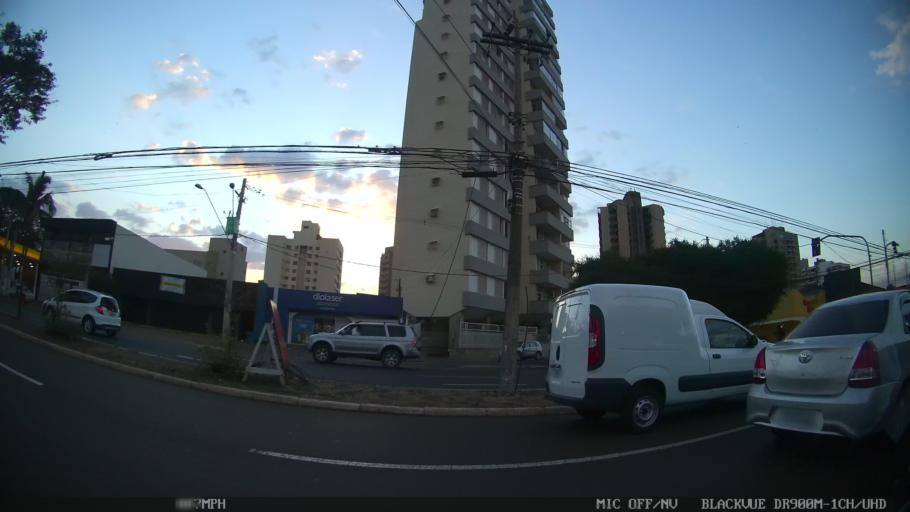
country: BR
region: Sao Paulo
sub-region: Ribeirao Preto
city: Ribeirao Preto
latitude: -21.1873
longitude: -47.8063
